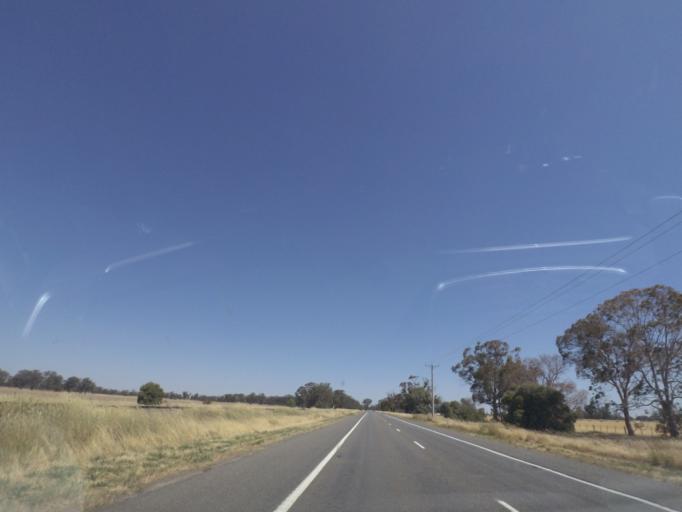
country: AU
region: Victoria
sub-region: Greater Shepparton
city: Shepparton
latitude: -36.2206
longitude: 145.4318
